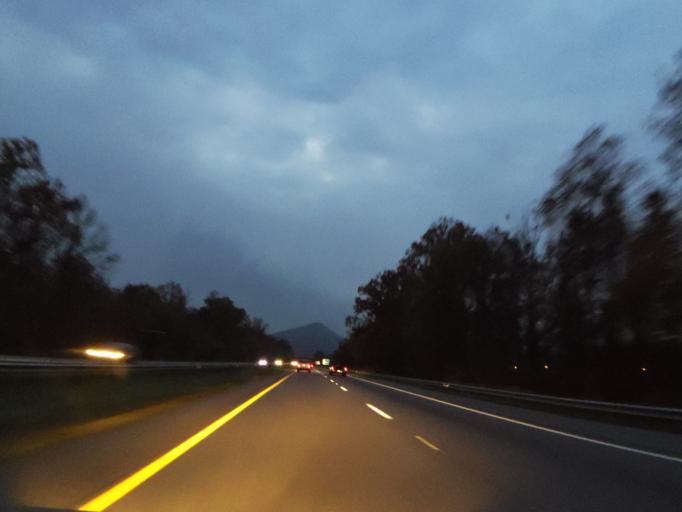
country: US
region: North Carolina
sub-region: McDowell County
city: West Marion
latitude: 35.6329
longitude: -82.1671
